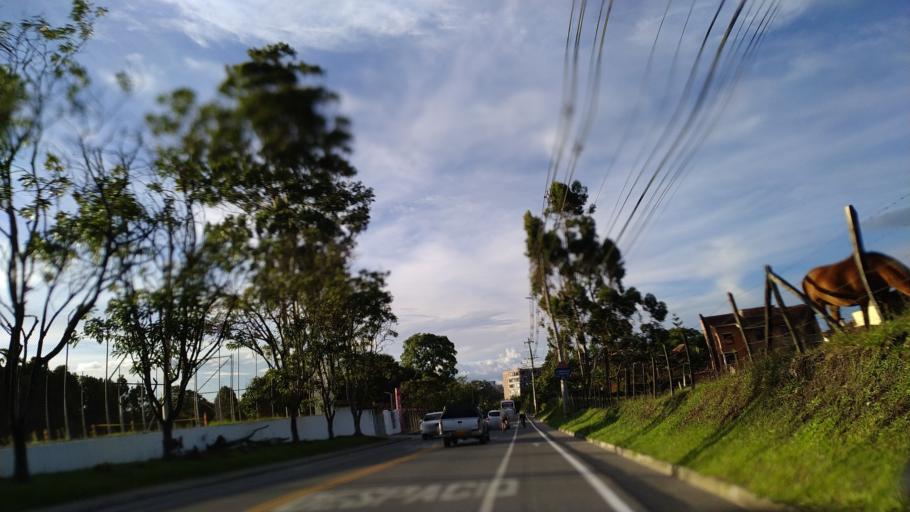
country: CO
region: Antioquia
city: Rionegro
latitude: 6.1363
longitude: -75.3782
